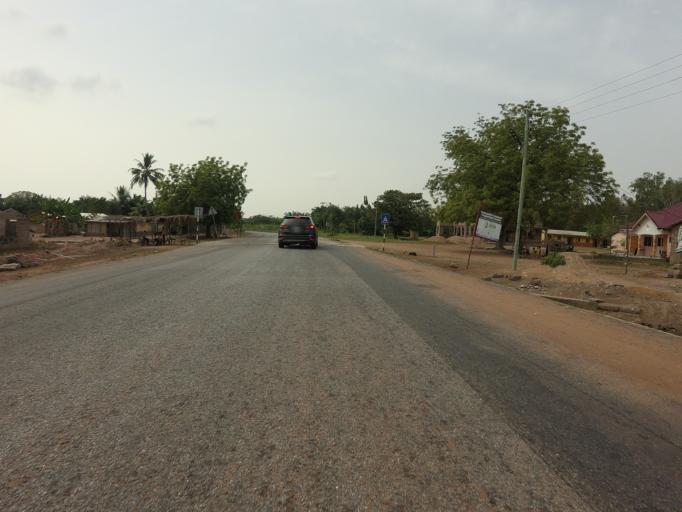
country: GH
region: Volta
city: Ho
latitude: 6.4317
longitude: 0.1907
